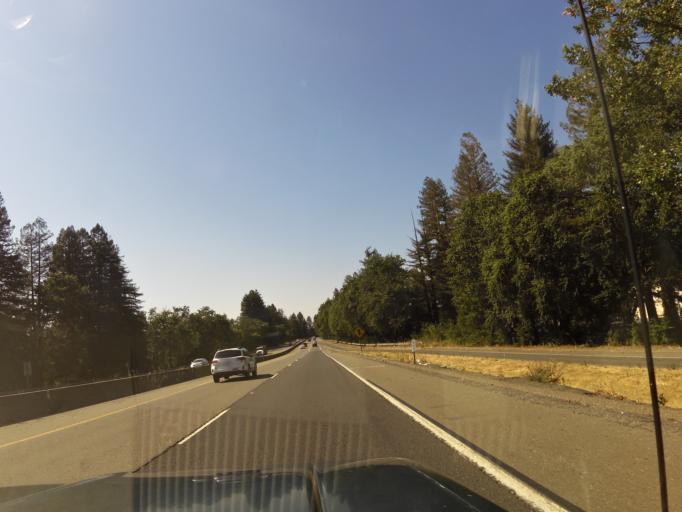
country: US
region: California
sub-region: Sonoma County
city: Healdsburg
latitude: 38.6084
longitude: -122.8739
